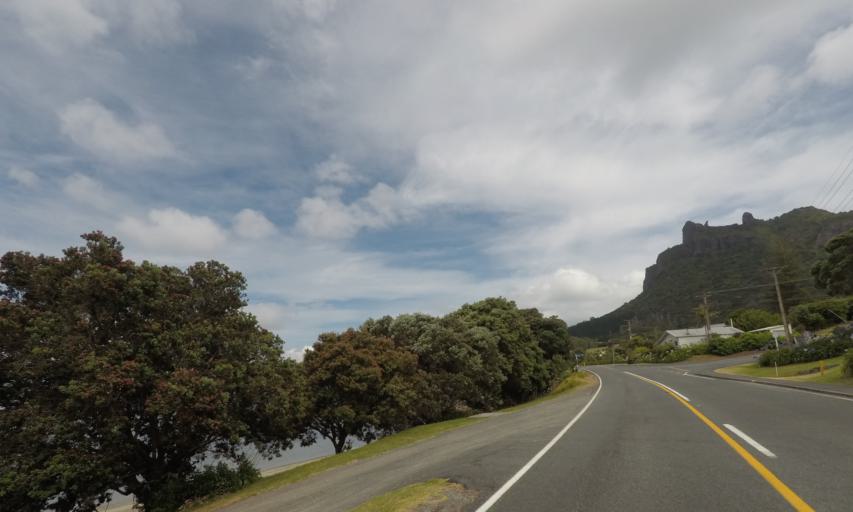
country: NZ
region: Northland
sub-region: Whangarei
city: Ruakaka
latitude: -35.8272
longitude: 174.5284
